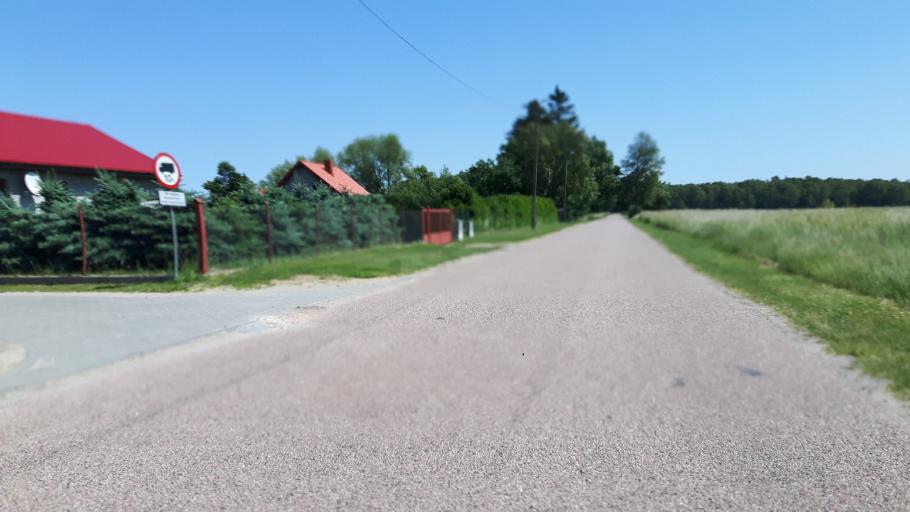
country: PL
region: Pomeranian Voivodeship
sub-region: Powiat slupski
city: Smoldzino
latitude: 54.6868
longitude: 17.2868
